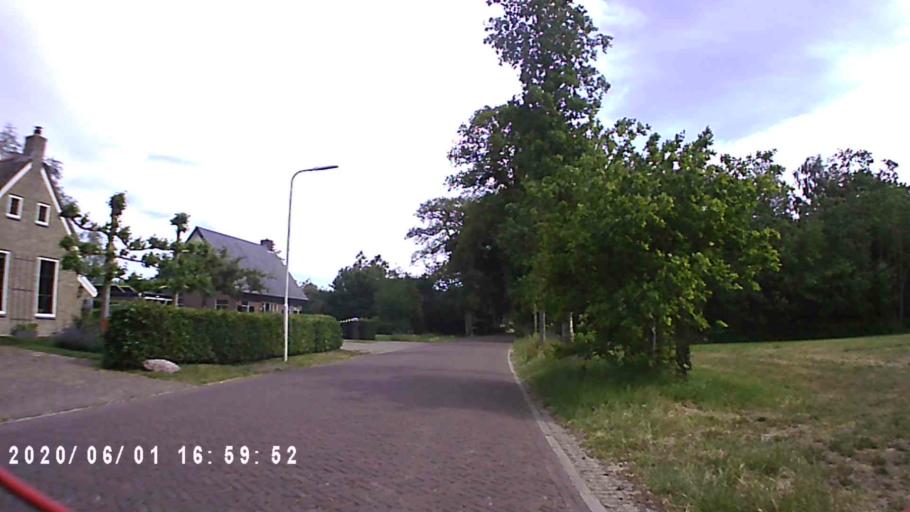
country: NL
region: Friesland
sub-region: Gemeente Tytsjerksteradiel
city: Hurdegaryp
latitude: 53.1847
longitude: 5.9289
